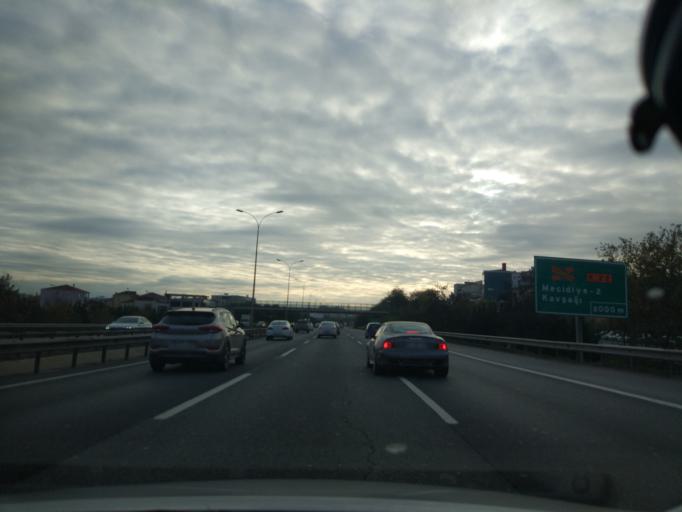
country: TR
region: Istanbul
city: Sultanbeyli
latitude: 40.9601
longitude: 29.2833
